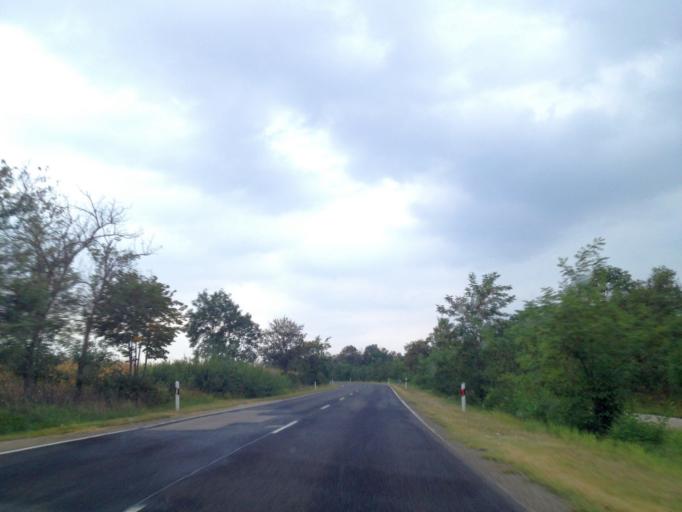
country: AT
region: Burgenland
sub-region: Politischer Bezirk Neusiedl am See
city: Nickelsdorf
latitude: 47.9254
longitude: 17.1264
